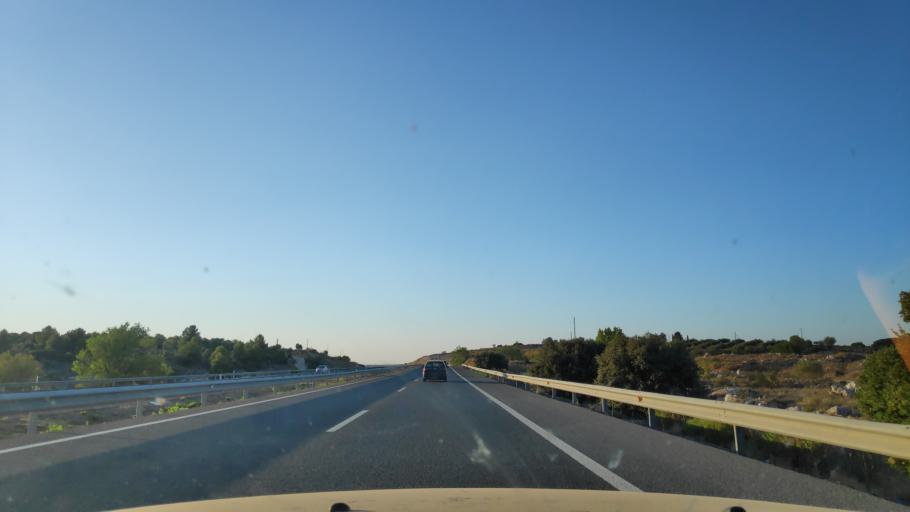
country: ES
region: Madrid
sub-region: Provincia de Madrid
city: Villarejo de Salvanes
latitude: 40.1860
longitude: -3.2979
